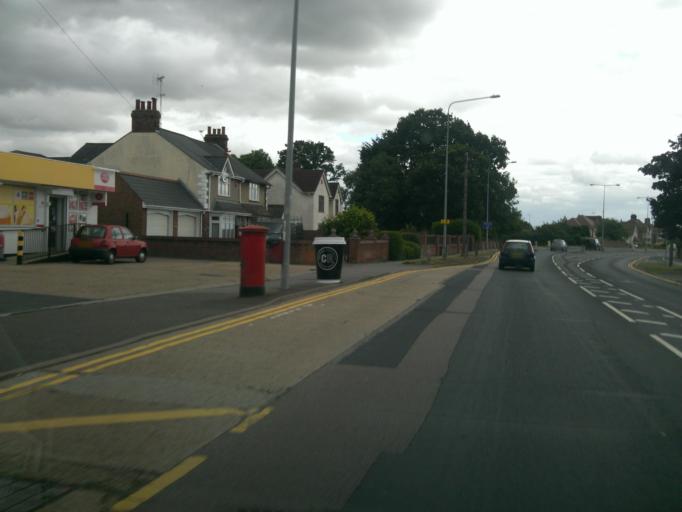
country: GB
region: England
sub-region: Essex
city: Colchester
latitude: 51.9031
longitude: 0.9239
